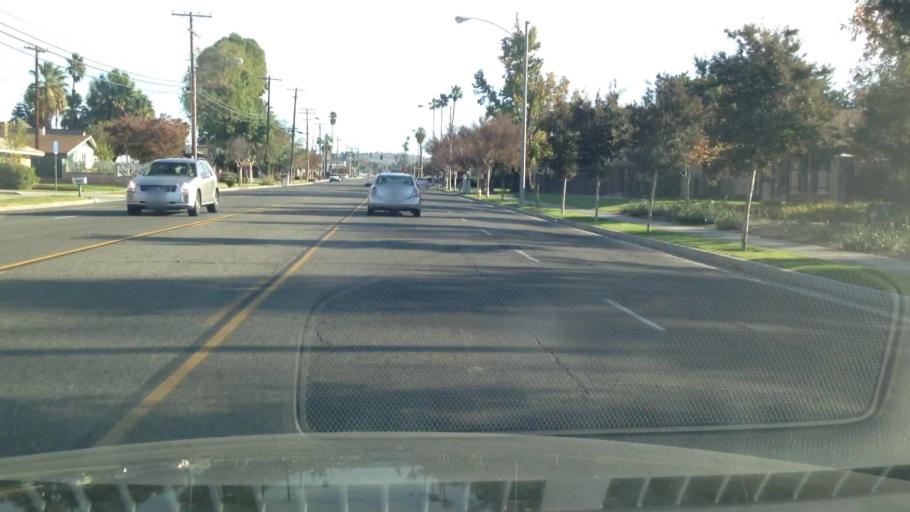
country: US
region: California
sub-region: Riverside County
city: Riverside
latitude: 33.9314
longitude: -117.4230
